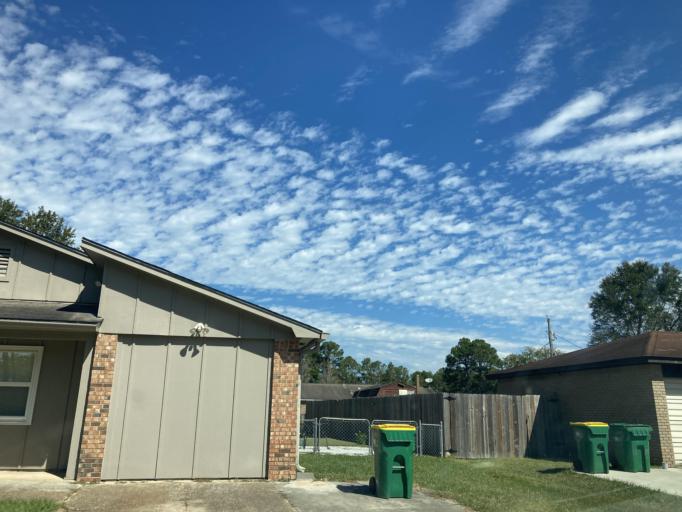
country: US
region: Mississippi
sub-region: Jackson County
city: Saint Martin
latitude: 30.4521
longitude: -88.8640
